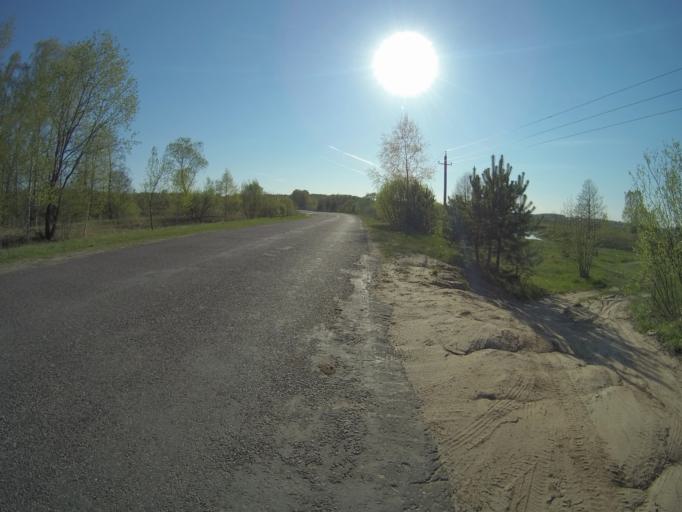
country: RU
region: Vladimir
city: Sudogda
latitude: 56.0633
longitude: 40.8328
